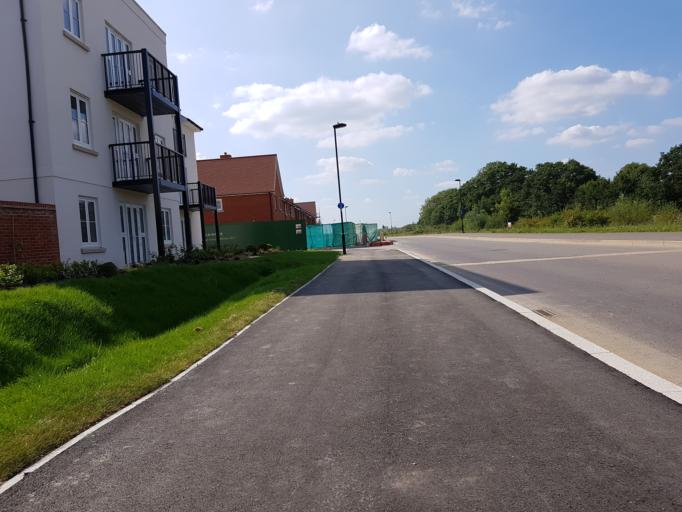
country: GB
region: England
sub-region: Hampshire
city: Waterlooville
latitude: 50.8819
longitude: -1.0395
